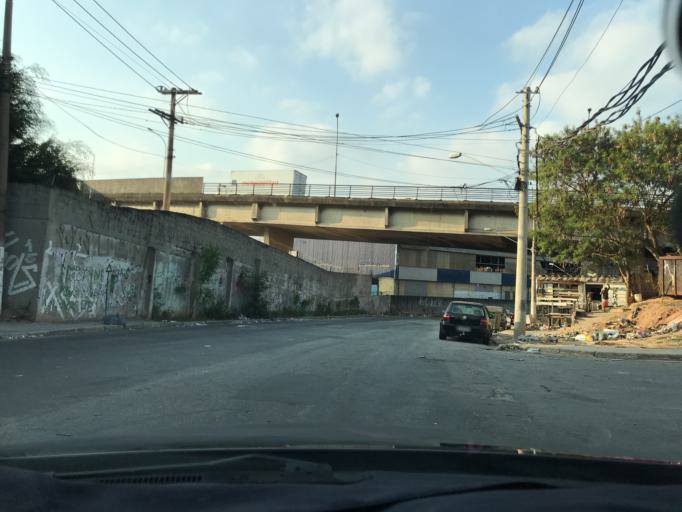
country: BR
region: Sao Paulo
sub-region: Osasco
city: Osasco
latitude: -23.5318
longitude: -46.7595
